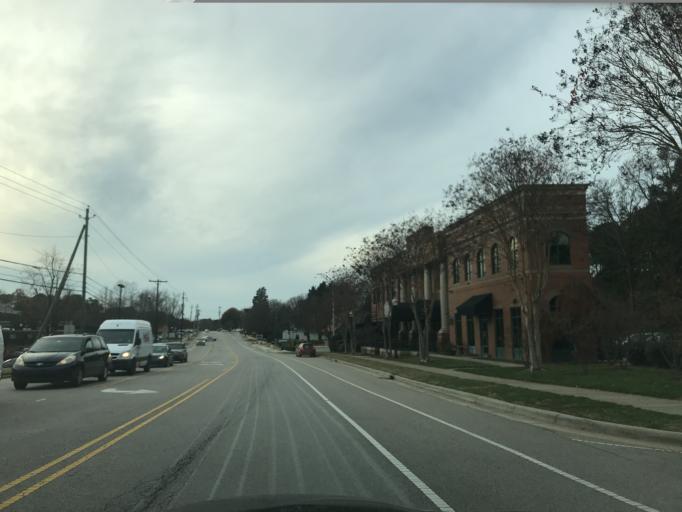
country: US
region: North Carolina
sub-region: Wake County
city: Cary
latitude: 35.7920
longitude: -78.7650
